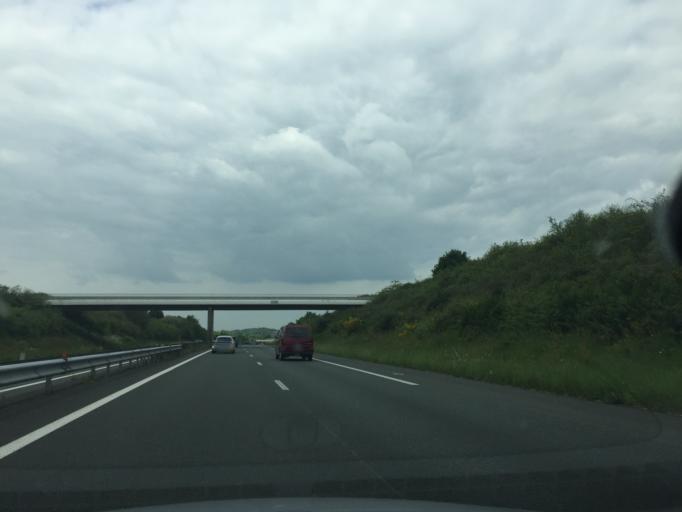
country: FR
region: Pays de la Loire
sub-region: Departement de la Vendee
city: Les Essarts
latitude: 46.7802
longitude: -1.1916
